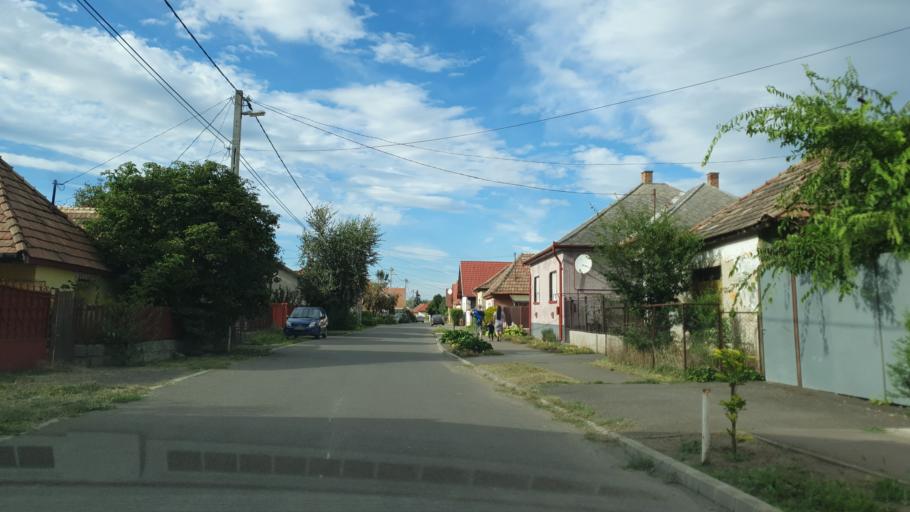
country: HU
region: Heves
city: Lorinci
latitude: 47.7421
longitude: 19.6753
